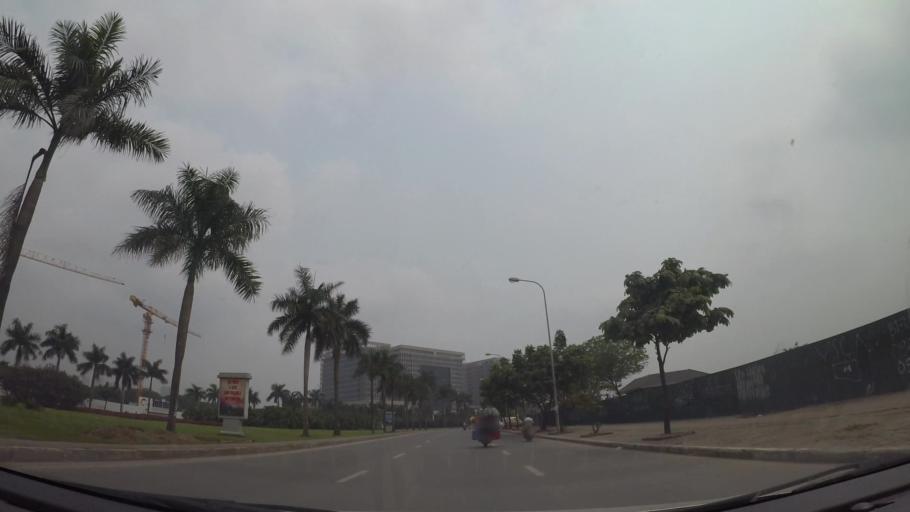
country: VN
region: Ha Noi
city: Cau Dien
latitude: 21.0094
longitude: 105.7728
